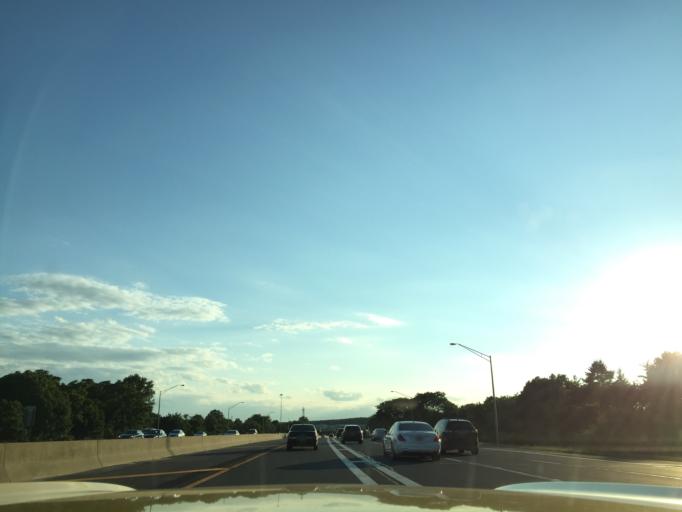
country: US
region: New York
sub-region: Suffolk County
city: Melville
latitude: 40.7819
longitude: -73.4101
